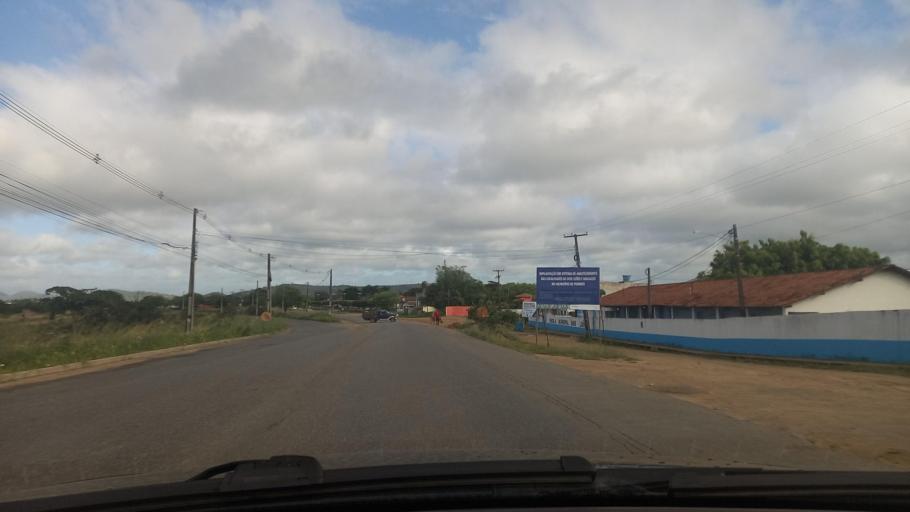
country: BR
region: Pernambuco
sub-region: Vitoria De Santo Antao
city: Vitoria de Santo Antao
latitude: -8.1257
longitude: -35.3444
